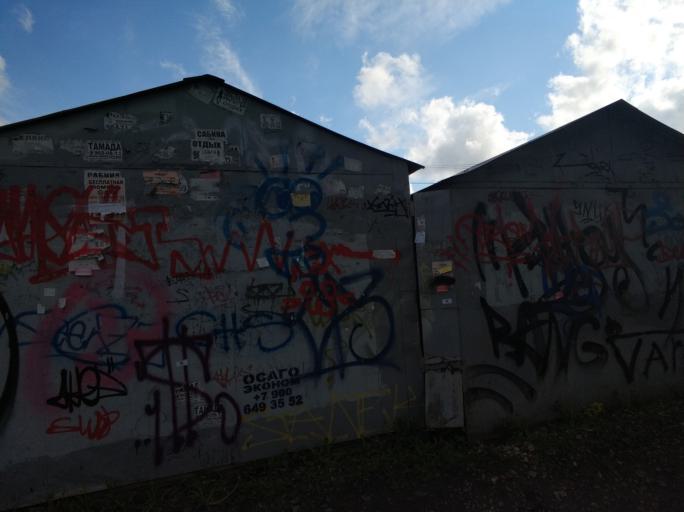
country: RU
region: Leningrad
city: Murino
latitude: 60.0431
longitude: 30.4301
